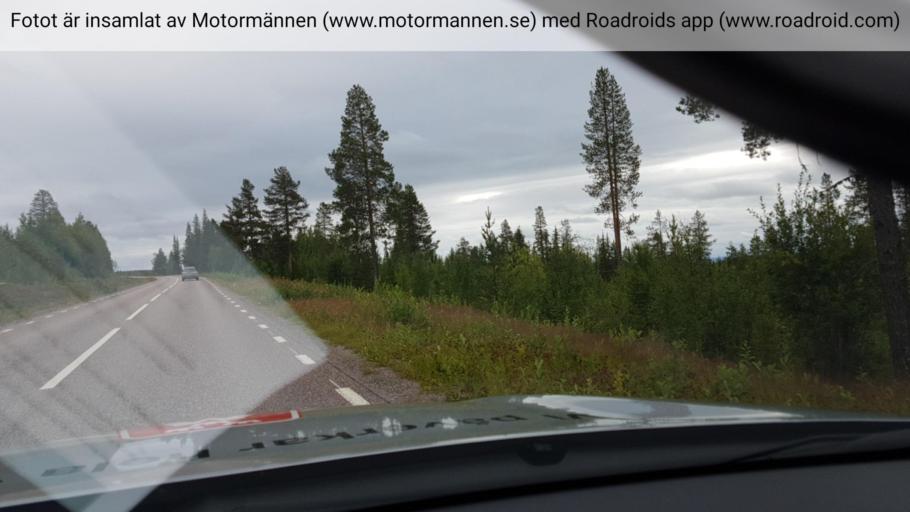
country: SE
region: Norrbotten
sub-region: Gallivare Kommun
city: Gaellivare
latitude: 67.0477
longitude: 21.6139
